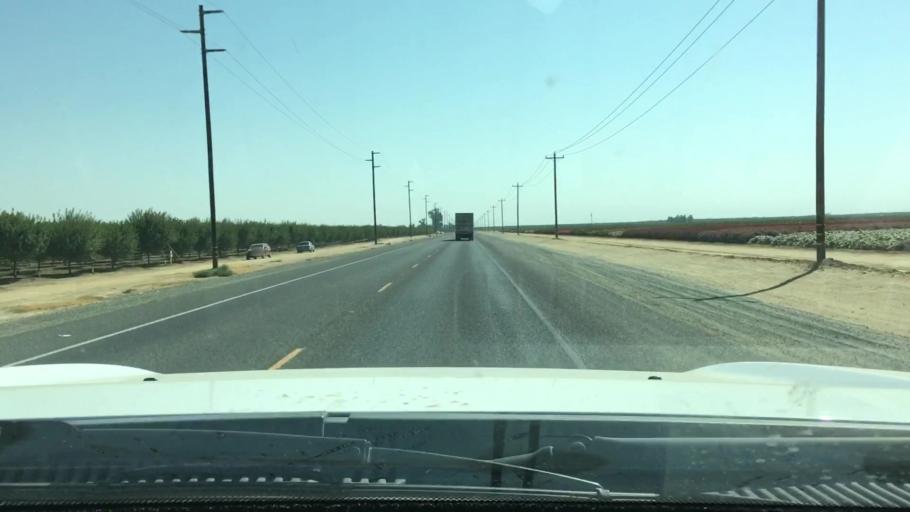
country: US
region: California
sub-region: Kern County
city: Lost Hills
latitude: 35.6011
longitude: -119.5440
